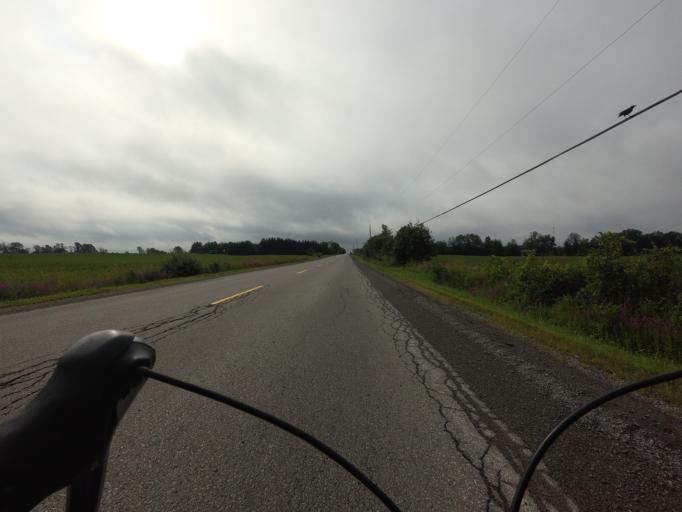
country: CA
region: Ontario
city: Bells Corners
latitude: 45.0946
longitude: -75.7602
